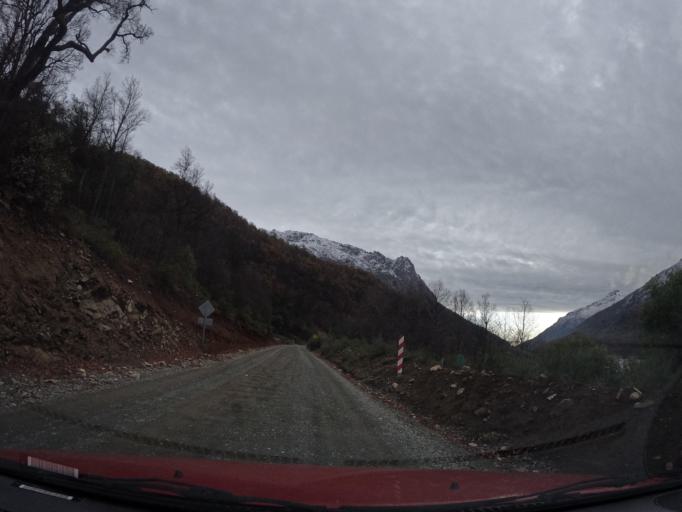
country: CL
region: Maule
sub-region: Provincia de Linares
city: Colbun
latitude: -35.8577
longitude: -71.1390
